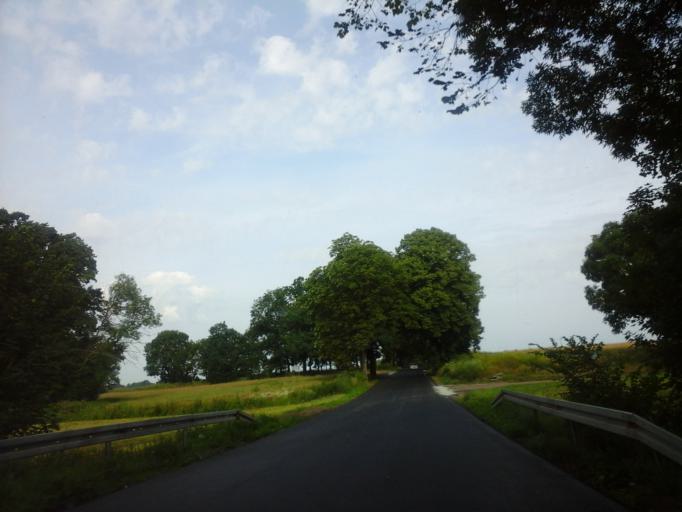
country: PL
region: West Pomeranian Voivodeship
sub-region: Powiat stargardzki
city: Stargard Szczecinski
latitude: 53.2716
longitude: 15.1294
